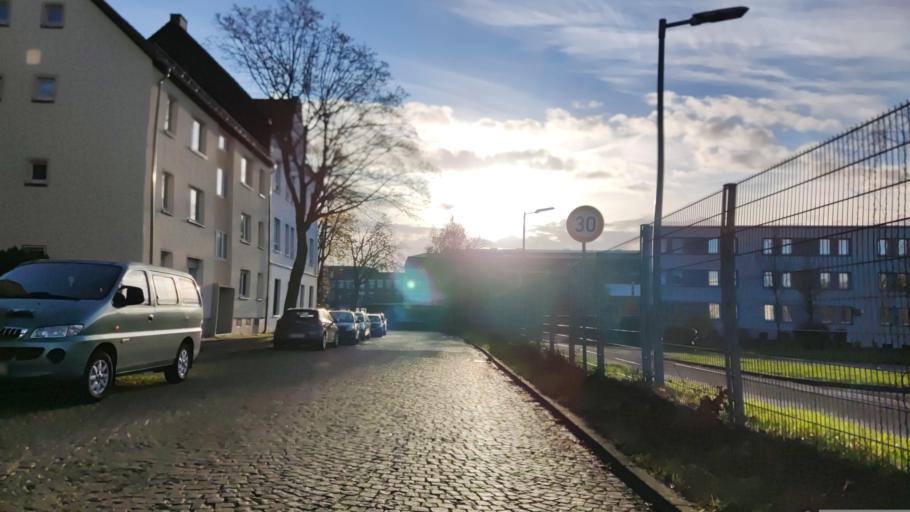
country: DE
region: North Rhine-Westphalia
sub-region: Regierungsbezirk Arnsberg
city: Bochum
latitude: 51.5064
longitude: 7.2057
